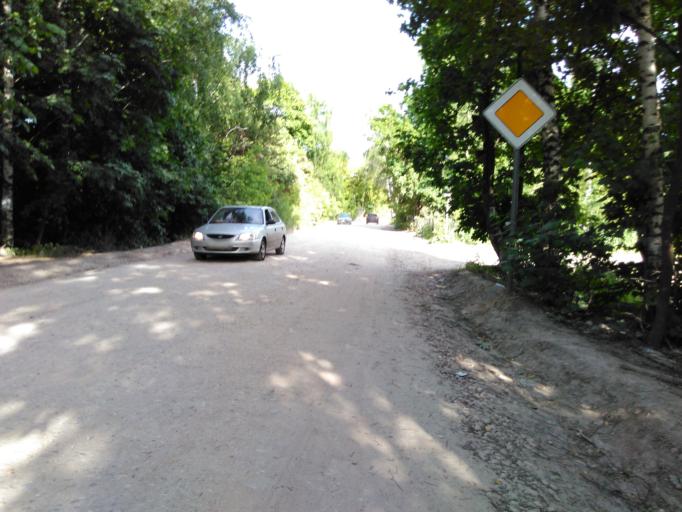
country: RU
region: Moskovskaya
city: Kupavna
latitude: 55.7531
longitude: 38.1242
